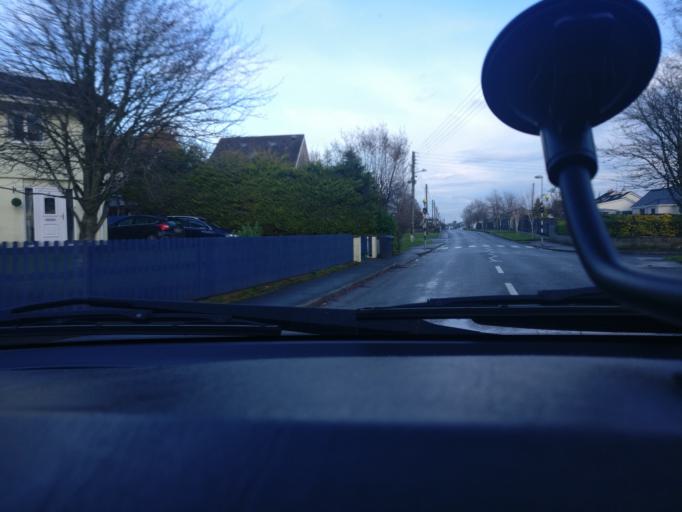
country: IE
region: Connaught
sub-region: County Galway
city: Loughrea
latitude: 53.1981
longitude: -8.5867
